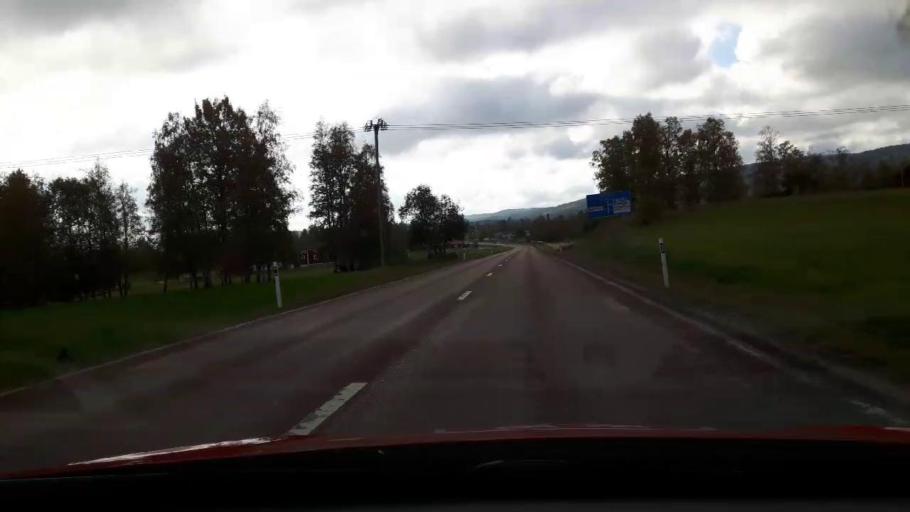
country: SE
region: Gaevleborg
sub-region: Ljusdals Kommun
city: Jaervsoe
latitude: 61.6778
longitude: 16.1452
